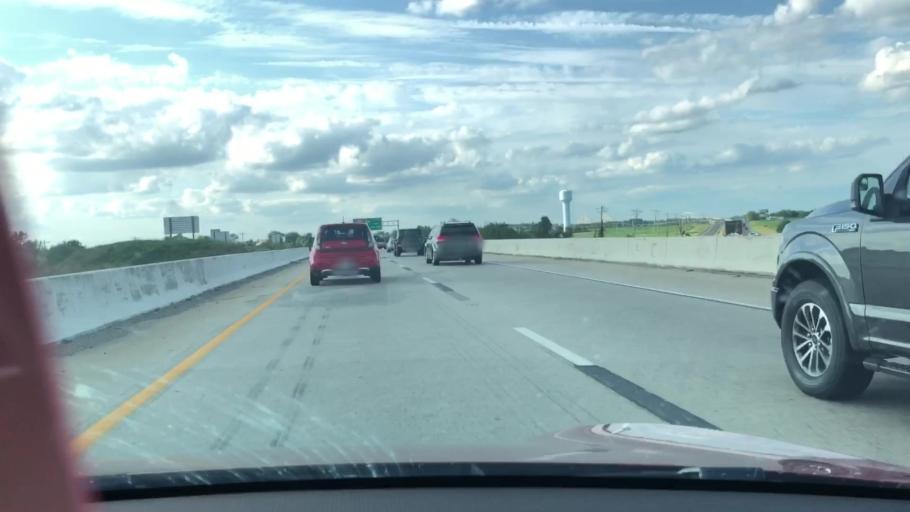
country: US
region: Delaware
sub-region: New Castle County
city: Delaware City
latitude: 39.5110
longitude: -75.6492
